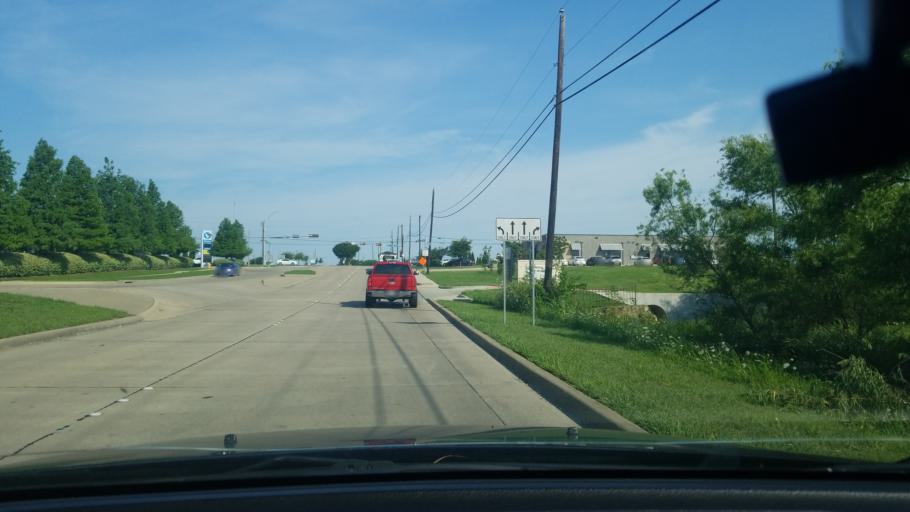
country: US
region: Texas
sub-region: Dallas County
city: Sunnyvale
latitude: 32.7787
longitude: -96.5646
